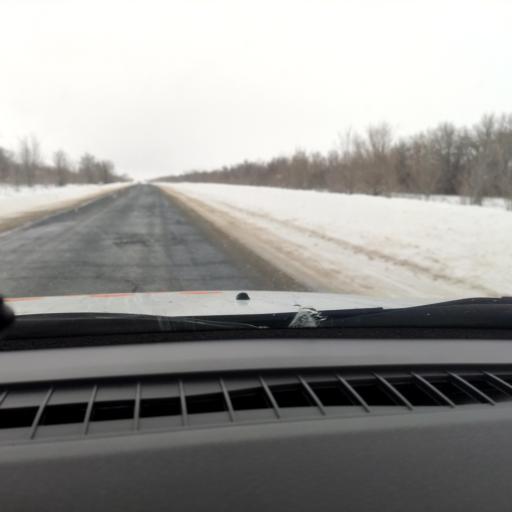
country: RU
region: Samara
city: Mayskoye
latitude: 52.4364
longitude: 50.5481
